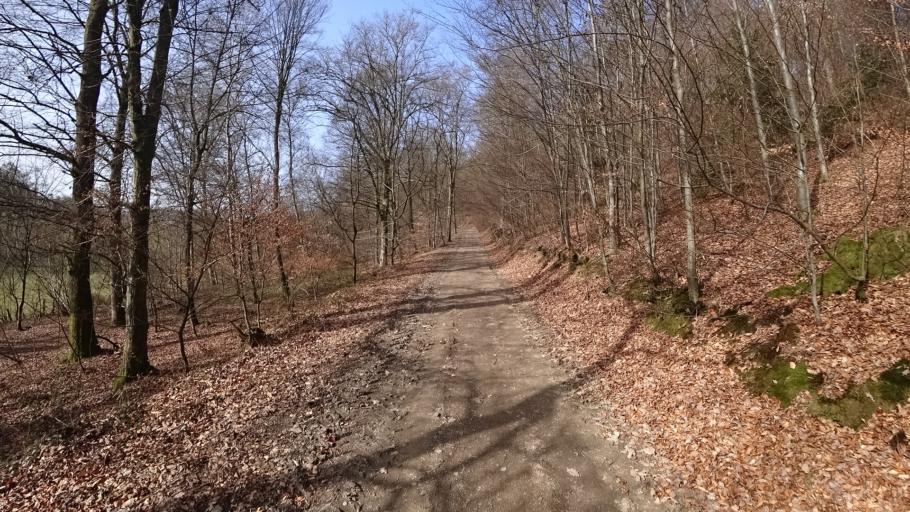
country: DE
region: Rheinland-Pfalz
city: Scheuerfeld
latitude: 50.7778
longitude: 7.8289
